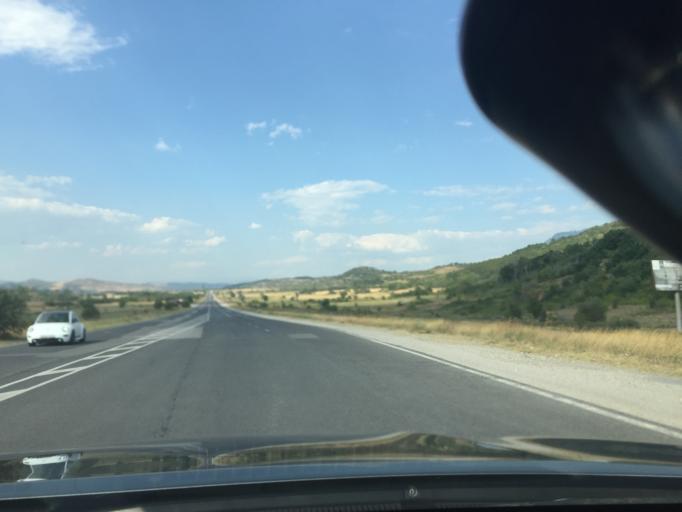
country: BG
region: Kyustendil
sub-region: Obshtina Boboshevo
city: Boboshevo
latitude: 42.1644
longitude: 23.0440
